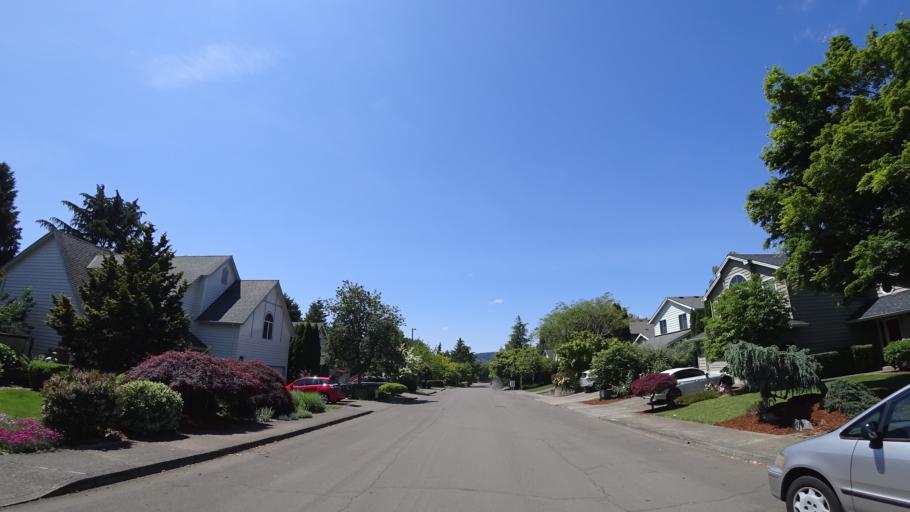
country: US
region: Oregon
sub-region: Washington County
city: Tigard
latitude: 45.4382
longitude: -122.8021
